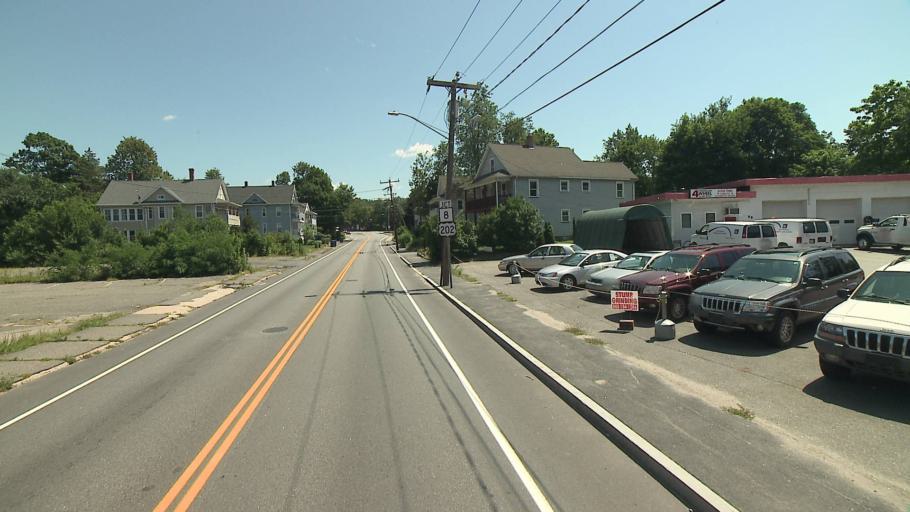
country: US
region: Connecticut
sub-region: Litchfield County
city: Torrington
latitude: 41.8085
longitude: -73.1165
